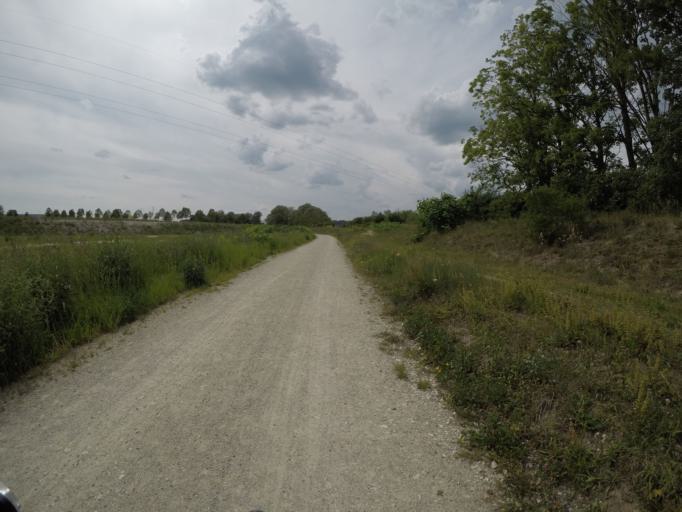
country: DE
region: Bavaria
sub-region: Lower Bavaria
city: Tiefenbach
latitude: 48.5419
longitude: 12.1118
